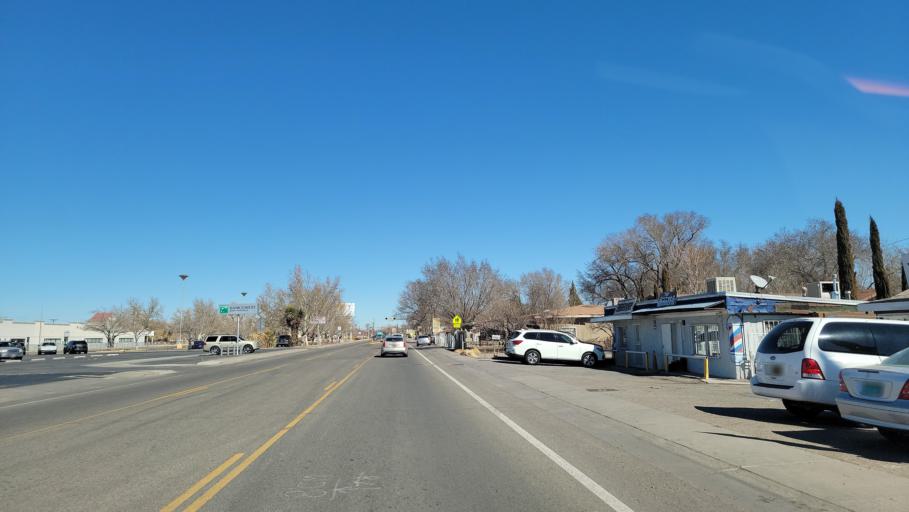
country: US
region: New Mexico
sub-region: Bernalillo County
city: South Valley
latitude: 35.0211
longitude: -106.6825
